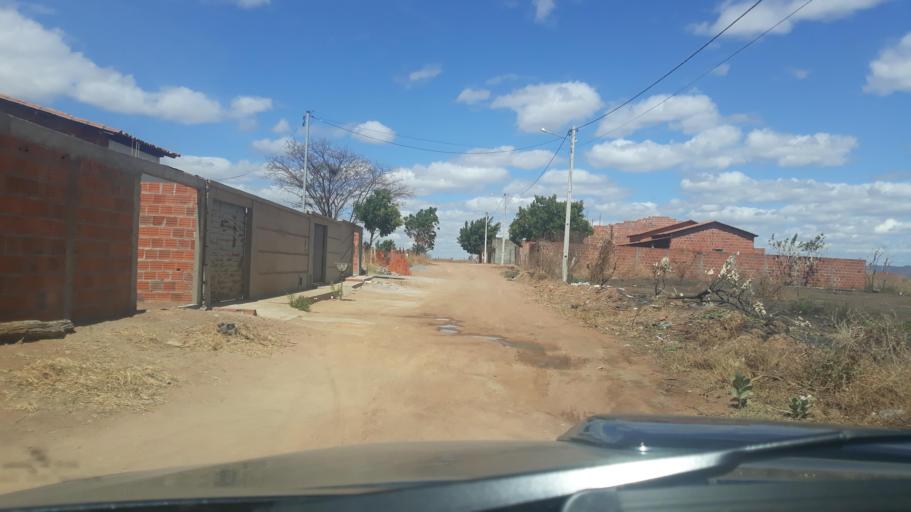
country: BR
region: Bahia
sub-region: Riacho De Santana
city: Riacho de Santana
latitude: -13.9021
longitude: -42.8517
